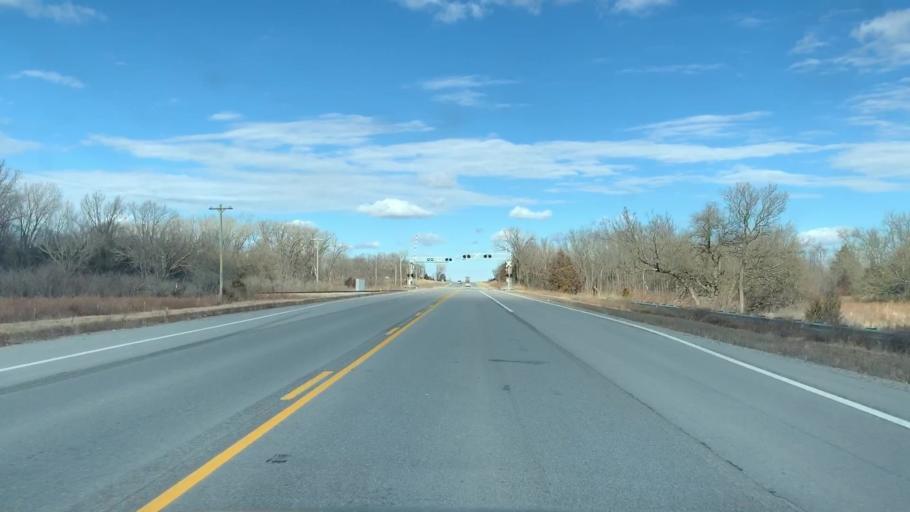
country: US
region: Kansas
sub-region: Cherokee County
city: Columbus
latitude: 37.3198
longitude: -94.8322
